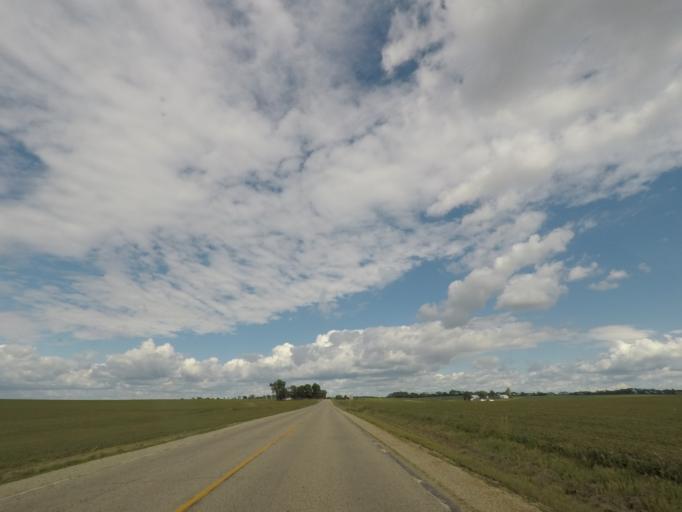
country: US
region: Wisconsin
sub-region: Rock County
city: Orfordville
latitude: 42.7047
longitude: -89.1576
